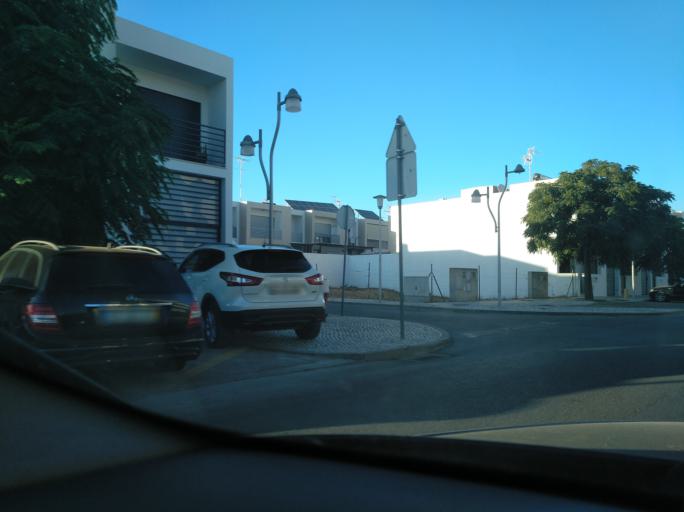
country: PT
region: Faro
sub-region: Vila Real de Santo Antonio
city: Vila Real de Santo Antonio
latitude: 37.1978
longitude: -7.4216
